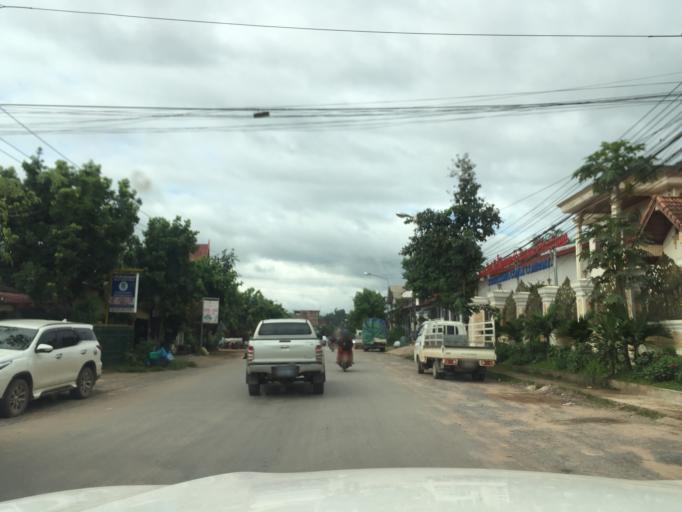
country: LA
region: Oudomxai
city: Muang Xay
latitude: 20.6973
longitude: 101.9892
